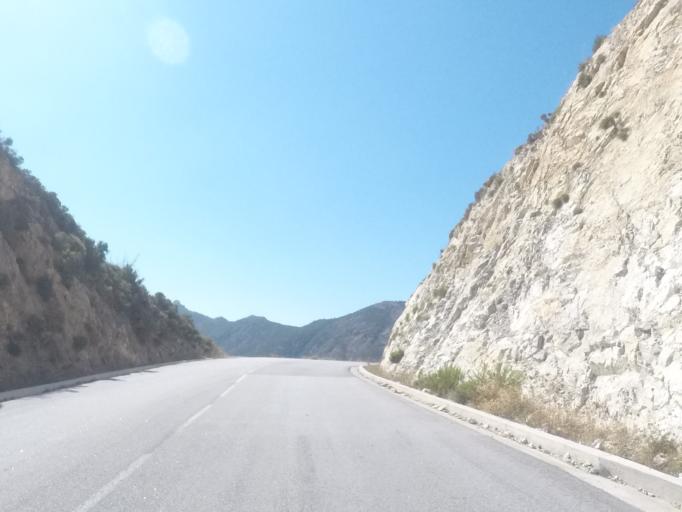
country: FR
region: Corsica
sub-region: Departement de la Haute-Corse
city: Calvi
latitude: 42.4759
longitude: 8.7562
